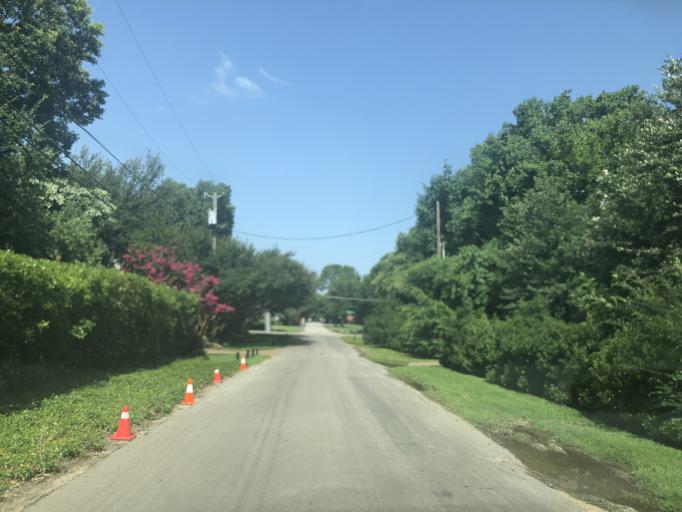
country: US
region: Texas
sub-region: Dallas County
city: University Park
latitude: 32.8771
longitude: -96.8130
